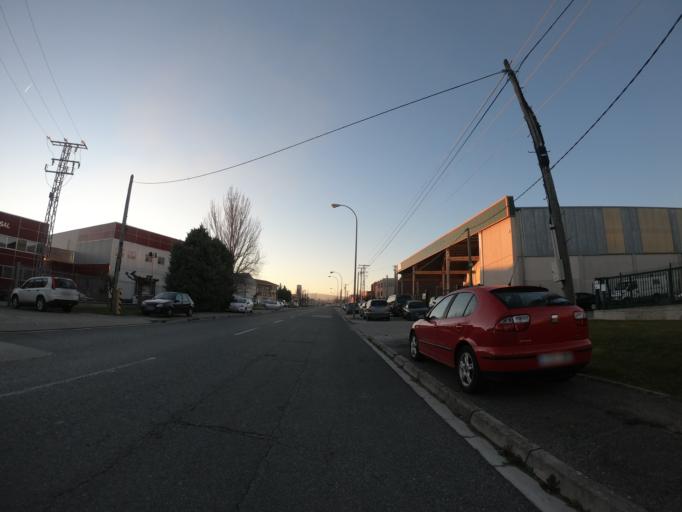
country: ES
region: Basque Country
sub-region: Provincia de Alava
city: Oyon
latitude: 42.4828
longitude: -2.4201
